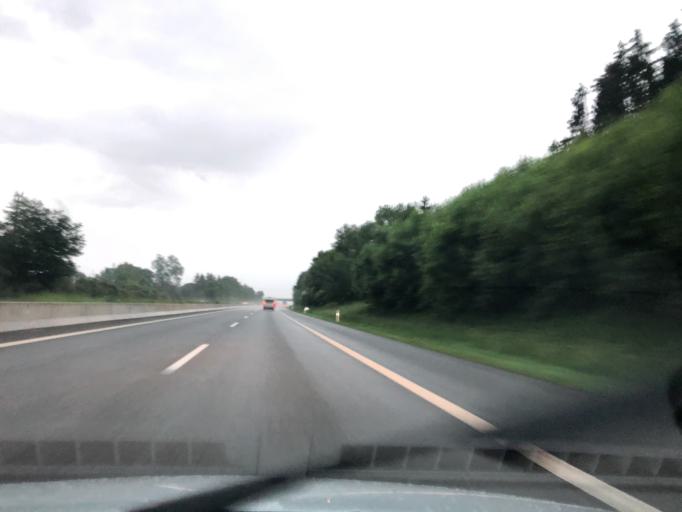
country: DE
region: Baden-Wuerttemberg
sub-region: Freiburg Region
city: Trossingen
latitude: 48.0653
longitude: 8.6128
